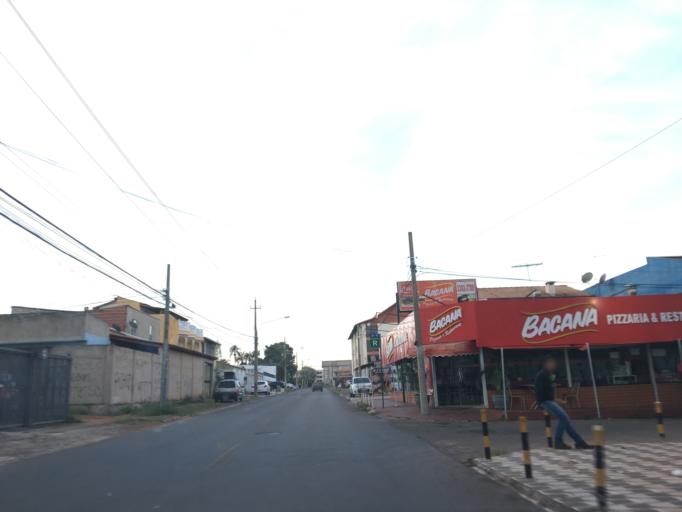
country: BR
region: Federal District
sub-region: Brasilia
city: Brasilia
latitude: -15.8173
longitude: -47.9771
